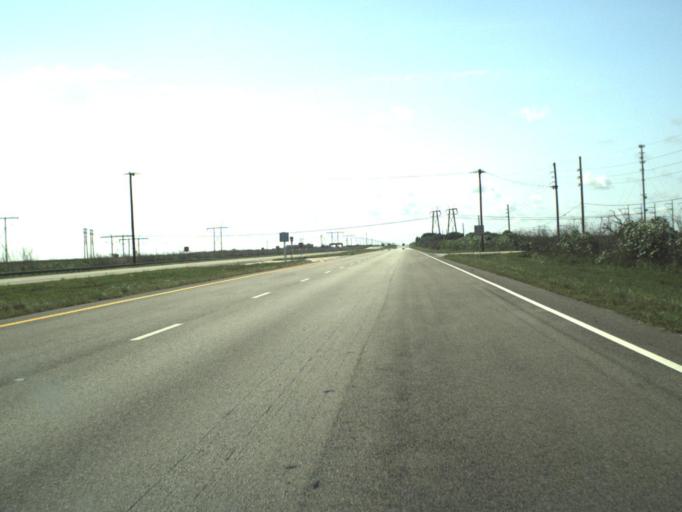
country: US
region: Florida
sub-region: Broward County
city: Weston
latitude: 26.3447
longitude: -80.5456
